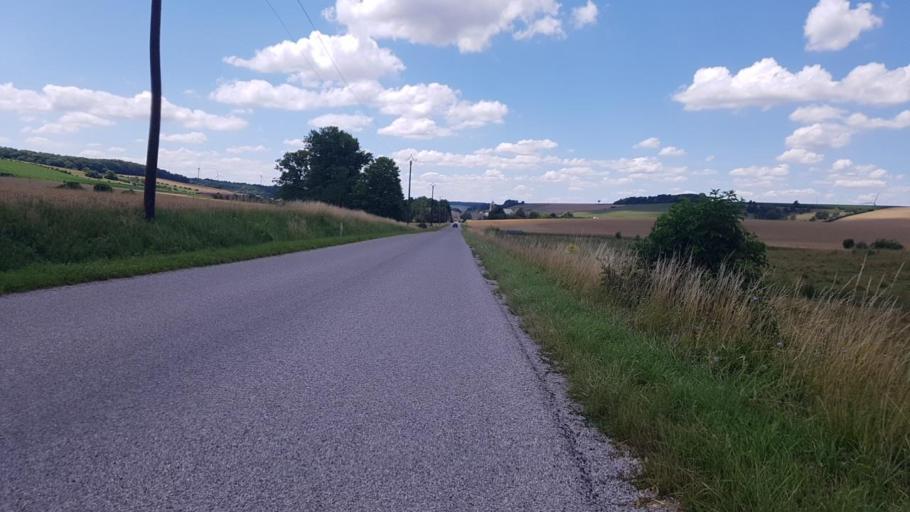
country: FR
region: Lorraine
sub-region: Departement de la Meuse
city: Vacon
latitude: 48.6493
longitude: 5.5222
